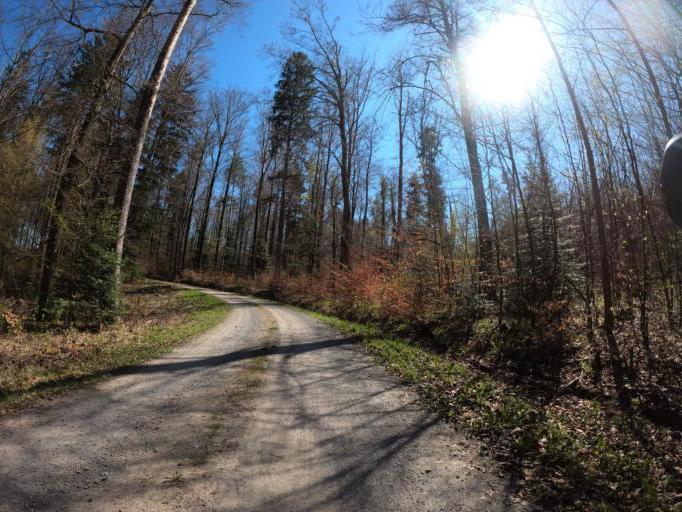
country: DE
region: Baden-Wuerttemberg
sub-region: Karlsruhe Region
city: Niefern-Oschelbronn
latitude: 48.8939
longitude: 8.7828
